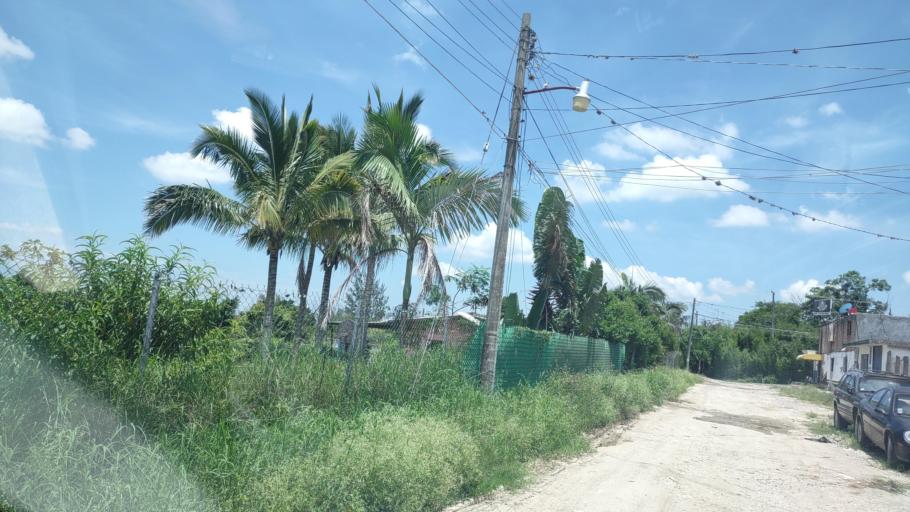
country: MX
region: Veracruz
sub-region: Emiliano Zapata
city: Dos Rios
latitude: 19.4928
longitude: -96.8131
